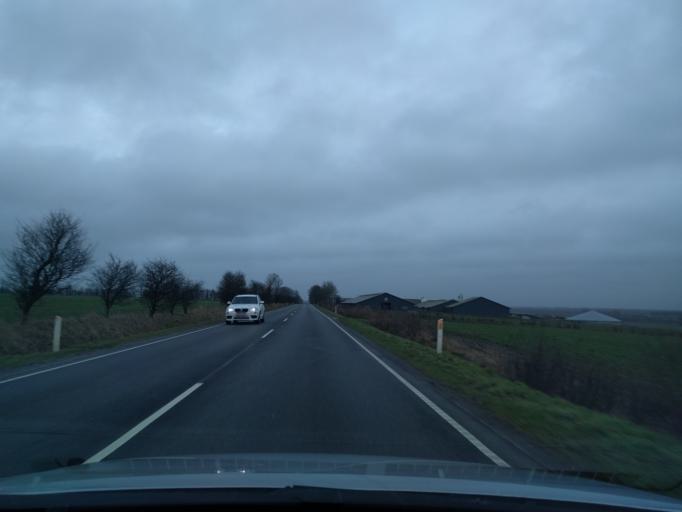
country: DK
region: South Denmark
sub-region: Tonder Kommune
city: Toftlund
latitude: 55.2514
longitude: 9.1618
